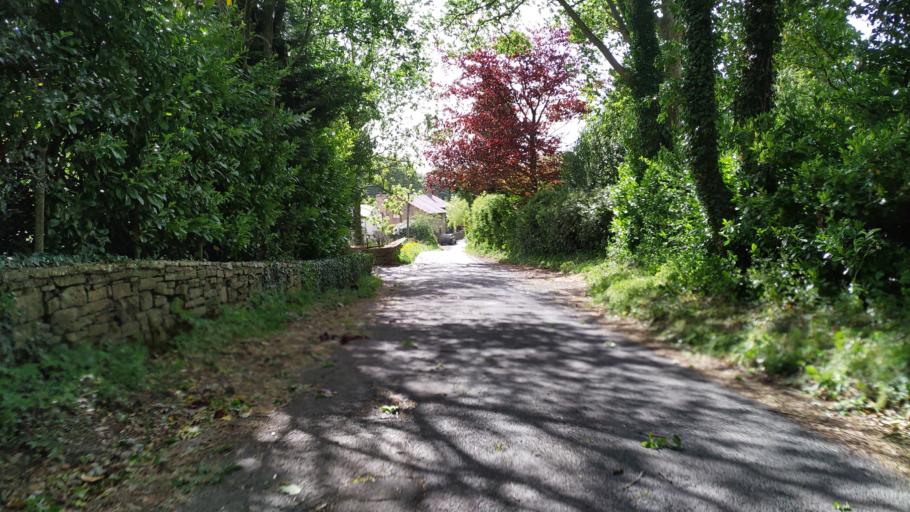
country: GB
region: England
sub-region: Lancashire
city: Chorley
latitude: 53.6450
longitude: -2.5936
